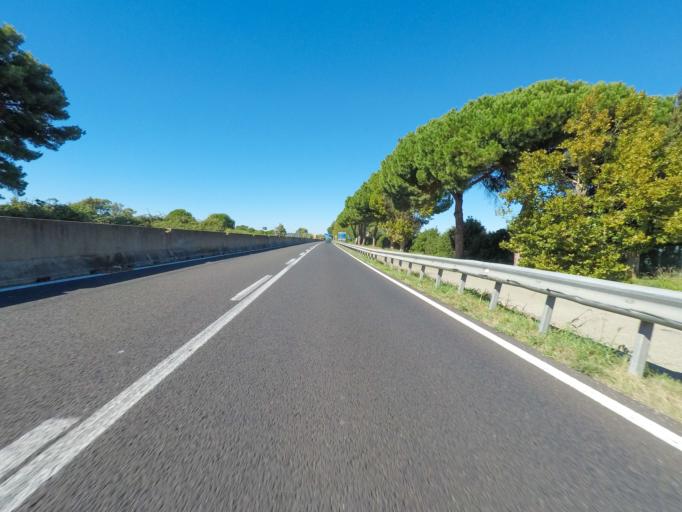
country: IT
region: Tuscany
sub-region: Provincia di Grosseto
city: Orbetello Scalo
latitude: 42.4685
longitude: 11.2385
